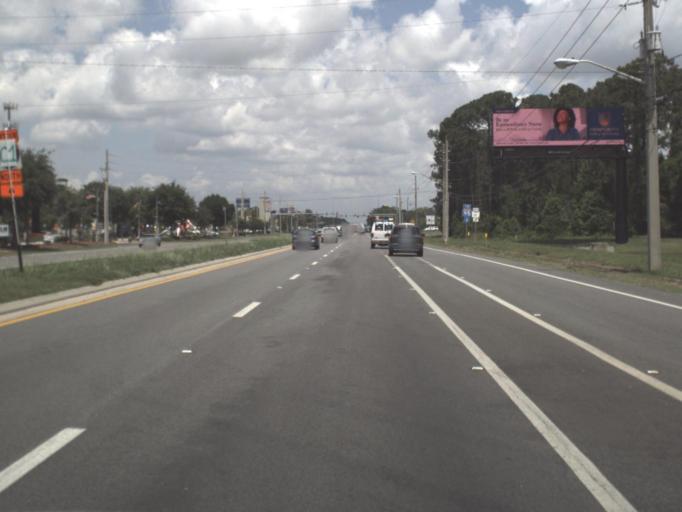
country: US
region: Florida
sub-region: Saint Johns County
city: Fruit Cove
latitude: 30.1762
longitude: -81.5493
